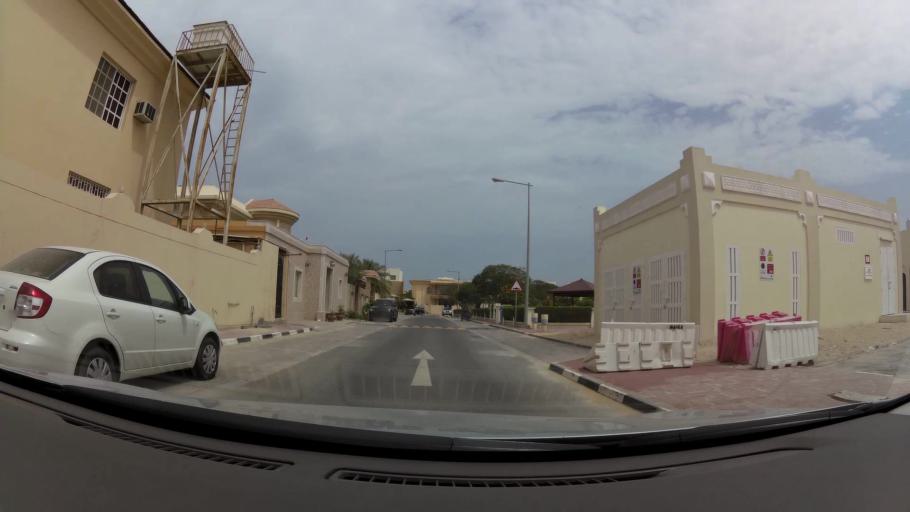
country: QA
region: Baladiyat ar Rayyan
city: Ar Rayyan
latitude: 25.3271
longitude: 51.4767
